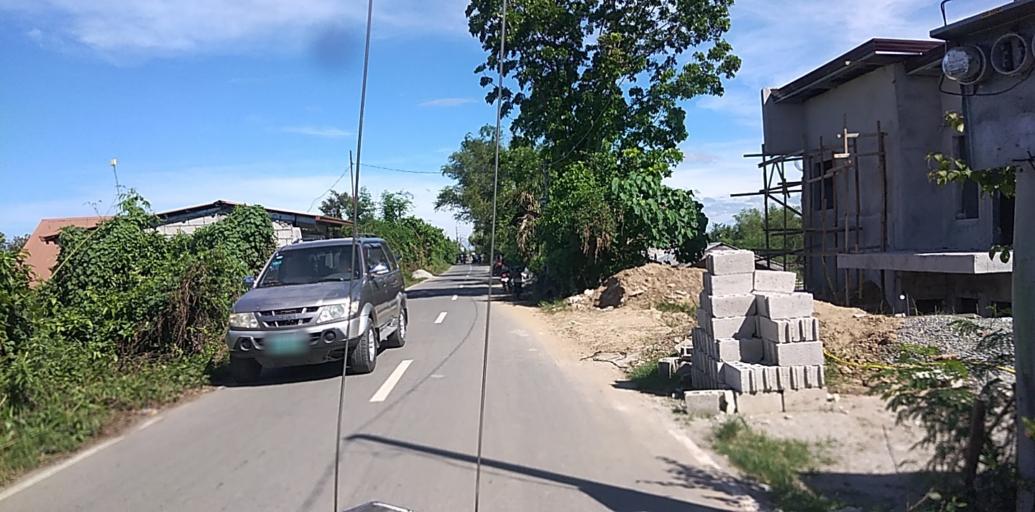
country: PH
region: Central Luzon
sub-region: Province of Pampanga
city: Candaba
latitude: 15.1029
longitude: 120.8150
